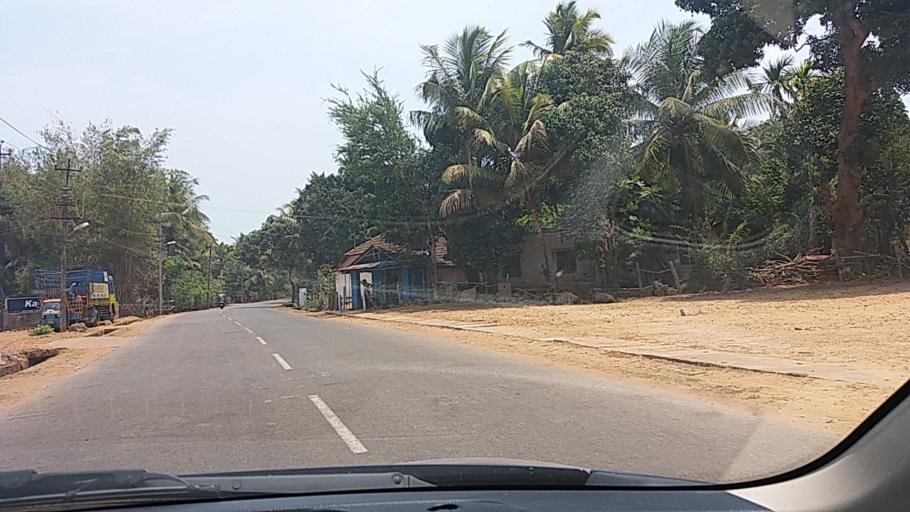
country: IN
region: Karnataka
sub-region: Uttar Kannada
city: Karwar
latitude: 14.8137
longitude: 74.1526
